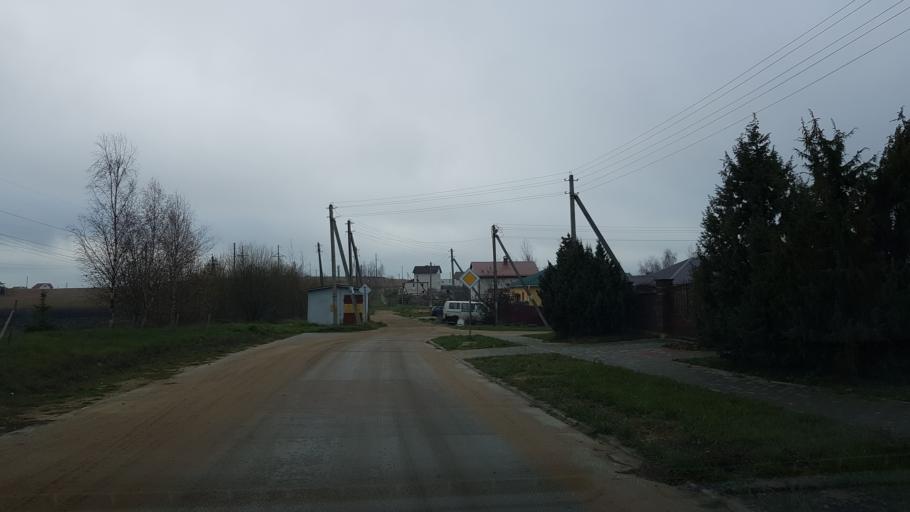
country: BY
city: Fanipol
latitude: 53.7308
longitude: 27.3168
